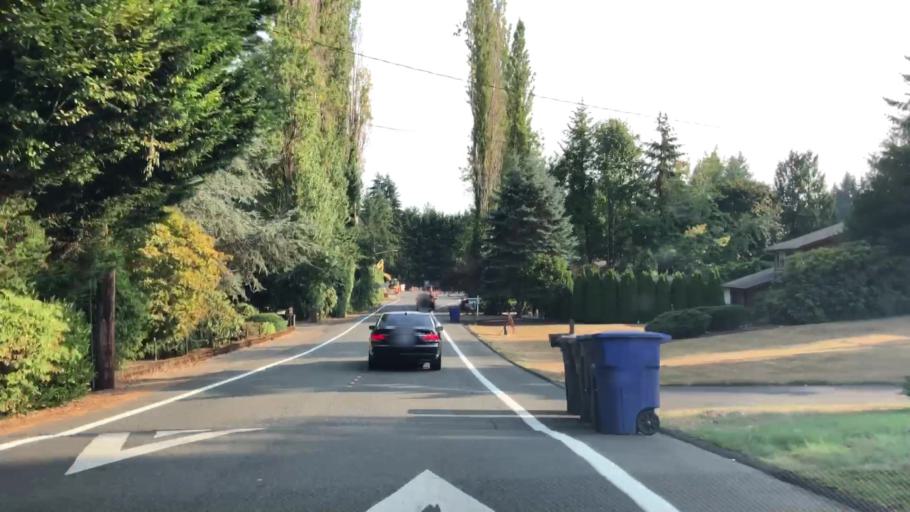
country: US
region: Washington
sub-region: King County
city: Bellevue
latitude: 47.6189
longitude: -122.1643
